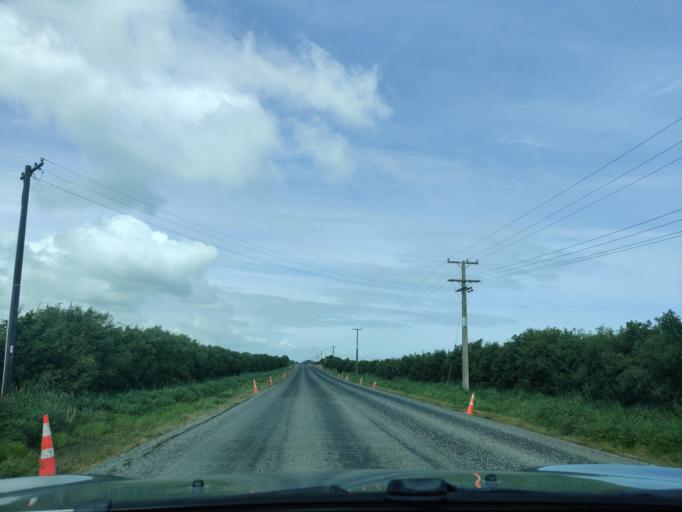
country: NZ
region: Taranaki
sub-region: South Taranaki District
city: Hawera
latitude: -39.5818
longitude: 174.2331
